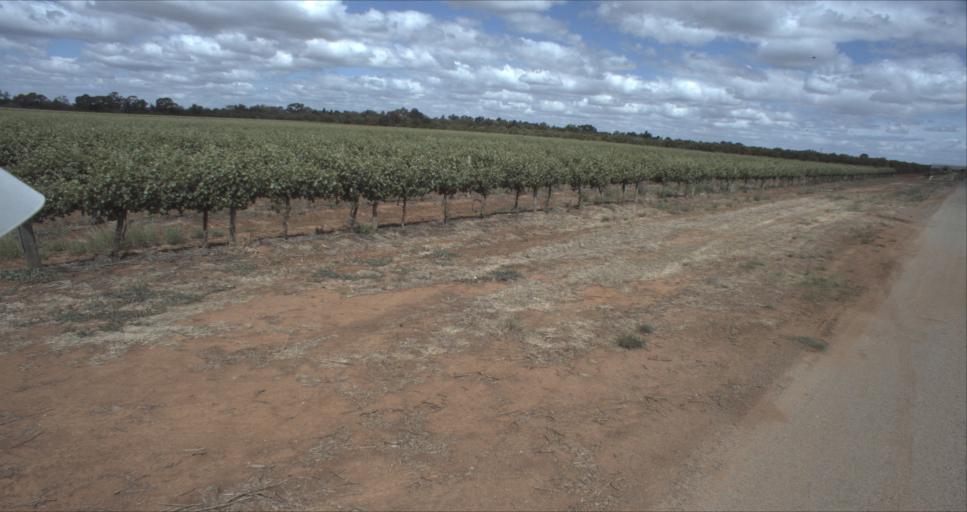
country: AU
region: New South Wales
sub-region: Leeton
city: Leeton
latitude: -34.5856
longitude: 146.3914
